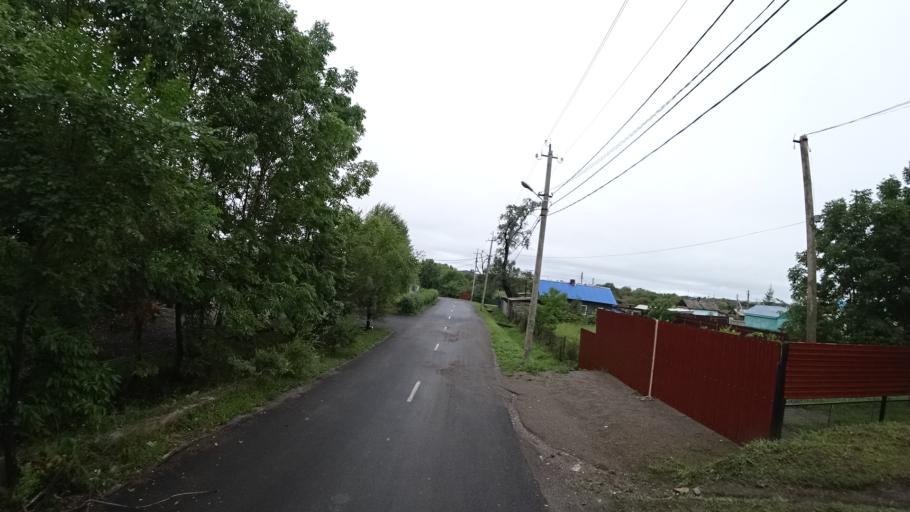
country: RU
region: Primorskiy
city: Monastyrishche
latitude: 44.2015
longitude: 132.4465
